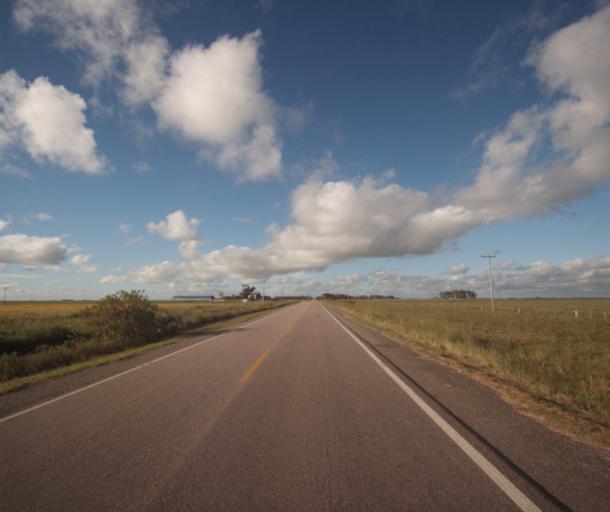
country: BR
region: Rio Grande do Sul
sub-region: Arroio Grande
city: Arroio Grande
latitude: -32.3828
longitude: -52.5536
